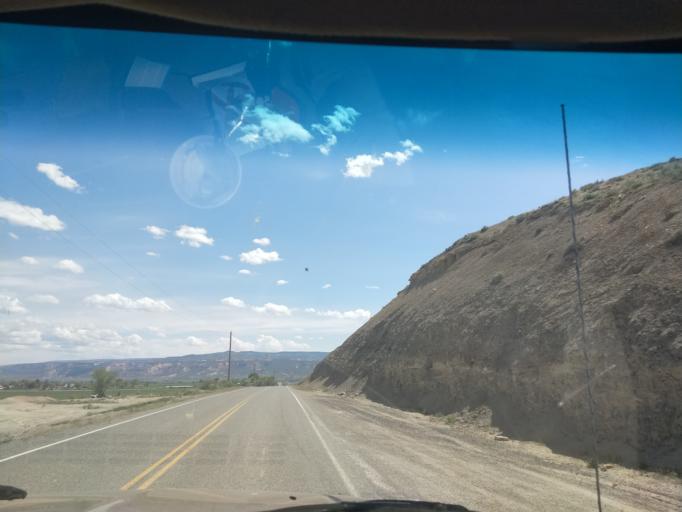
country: US
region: Colorado
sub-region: Mesa County
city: Fruita
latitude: 39.2054
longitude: -108.7570
